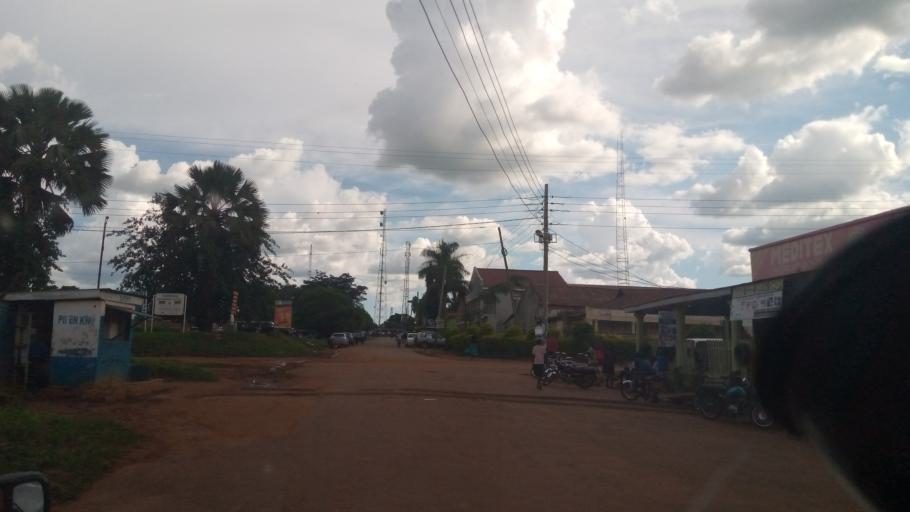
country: UG
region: Northern Region
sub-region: Lira District
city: Lira
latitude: 2.2411
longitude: 32.8969
